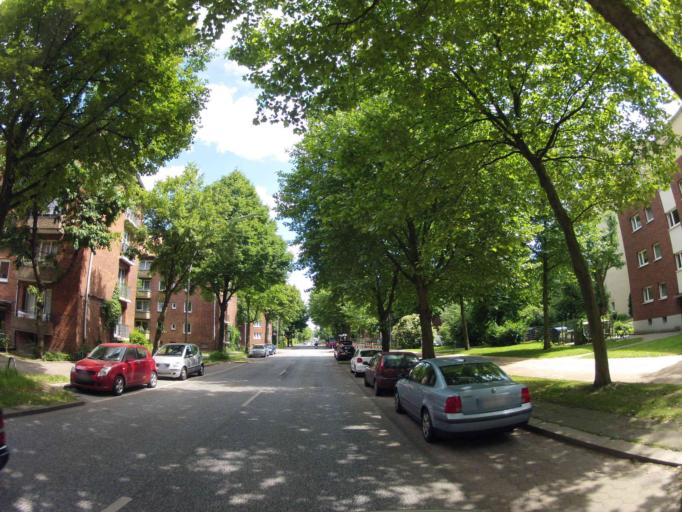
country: DE
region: Hamburg
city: Rothenburgsort
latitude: 53.5330
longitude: 10.0492
